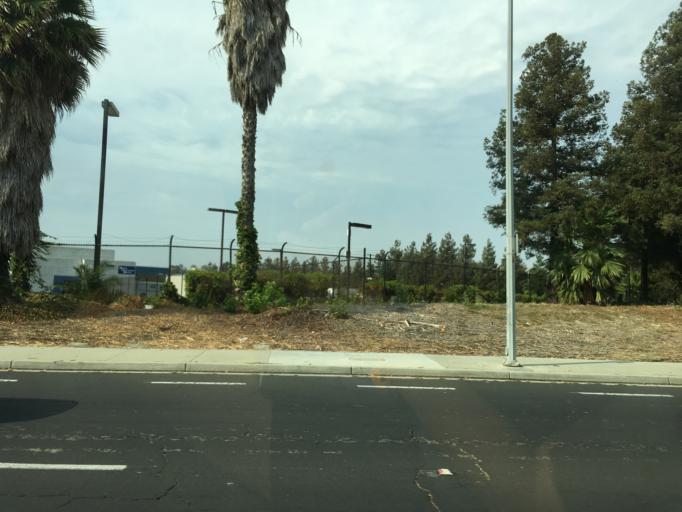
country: US
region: California
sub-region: Santa Clara County
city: Milpitas
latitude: 37.3879
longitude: -121.8844
